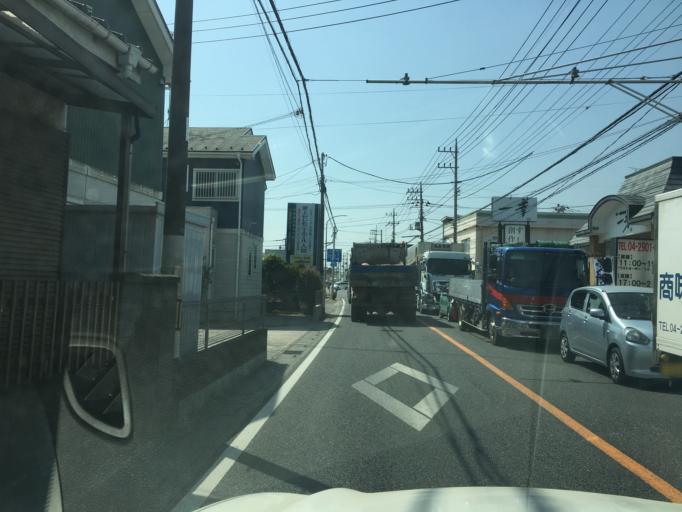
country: JP
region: Saitama
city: Sayama
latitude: 35.8238
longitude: 139.4091
